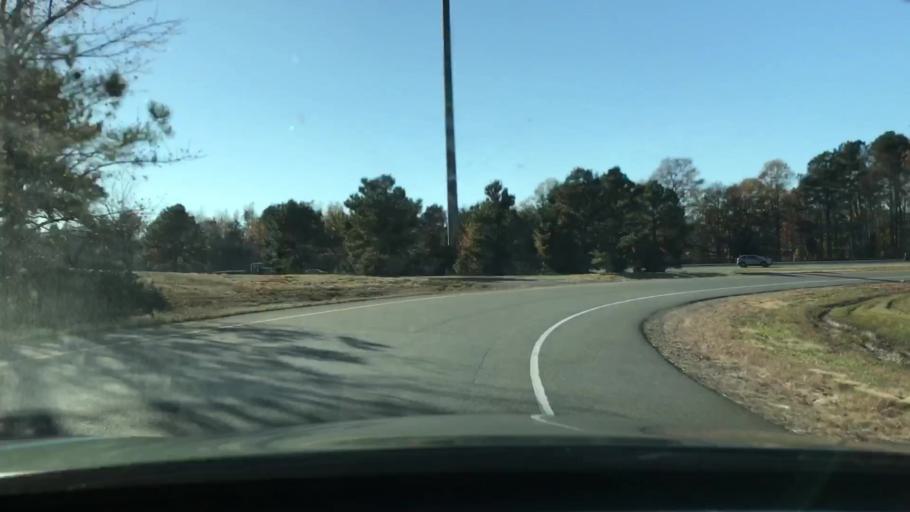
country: US
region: Virginia
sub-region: Henrico County
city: Chamberlayne
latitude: 37.6551
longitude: -77.4491
